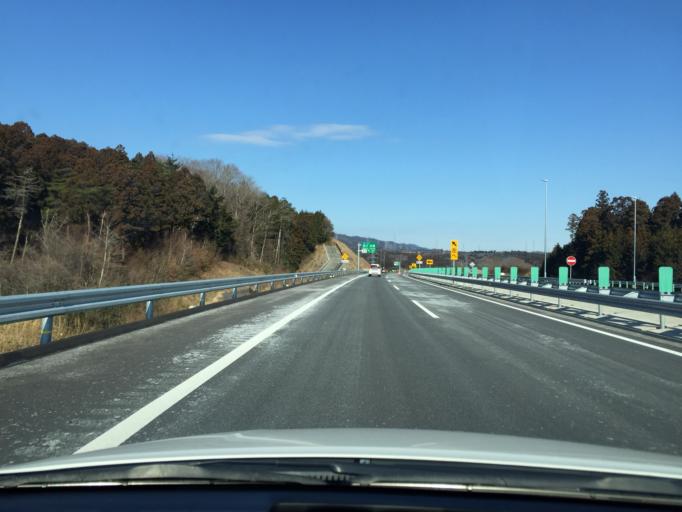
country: JP
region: Fukushima
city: Namie
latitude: 37.4958
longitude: 140.9441
